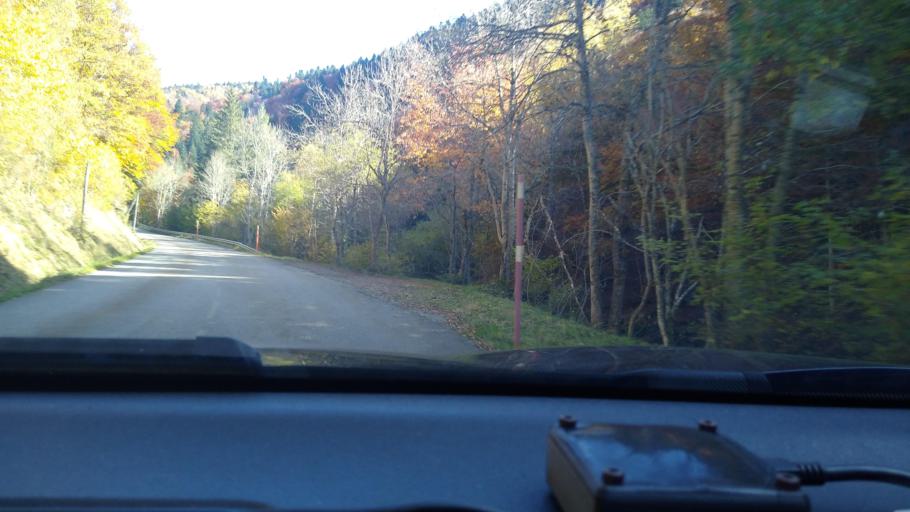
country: FR
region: Midi-Pyrenees
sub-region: Departement de l'Ariege
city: Ax-les-Thermes
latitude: 42.7167
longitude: 1.9202
